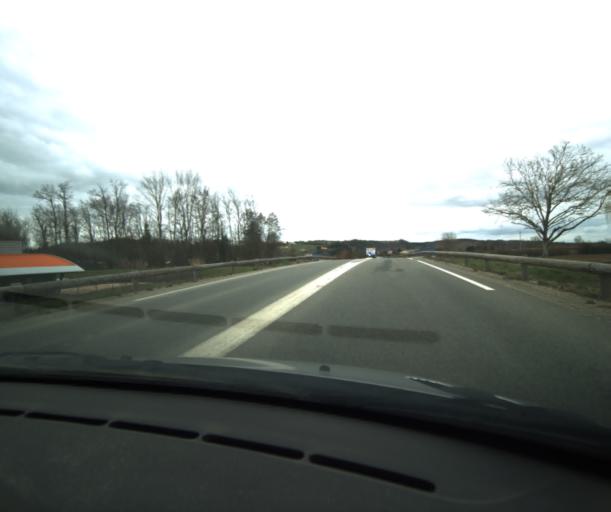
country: FR
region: Midi-Pyrenees
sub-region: Departement du Tarn-et-Garonne
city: Moissac
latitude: 44.1091
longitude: 1.1148
